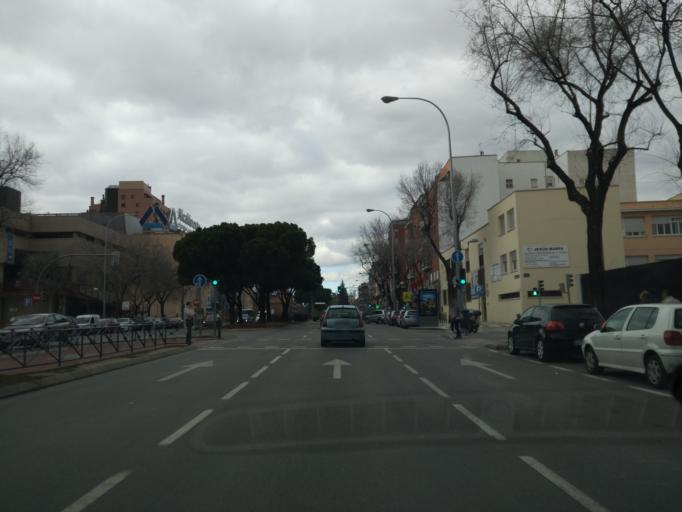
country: ES
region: Madrid
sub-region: Provincia de Madrid
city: San Blas
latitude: 40.4360
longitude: -3.6365
